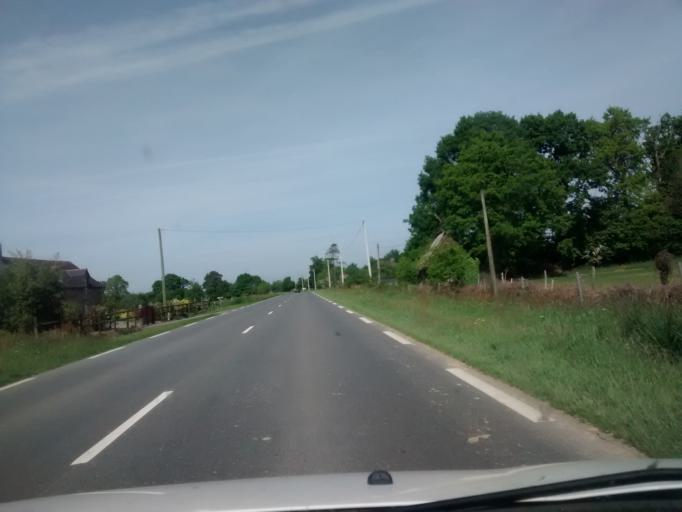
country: FR
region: Brittany
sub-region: Departement d'Ille-et-Vilaine
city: Saint-Brice-en-Cogles
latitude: 48.4207
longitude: -1.4038
